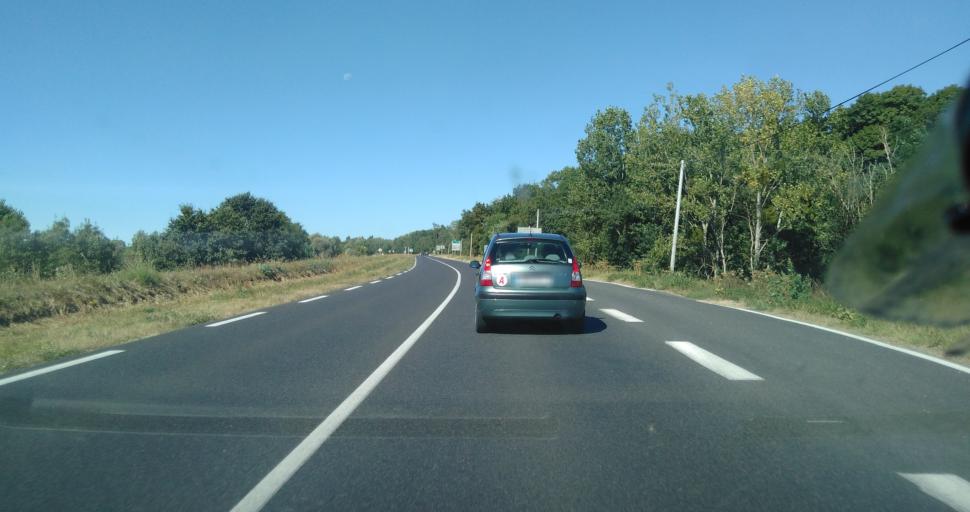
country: FR
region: Centre
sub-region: Departement d'Indre-et-Loire
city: Noizay
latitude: 47.4041
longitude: 0.9026
